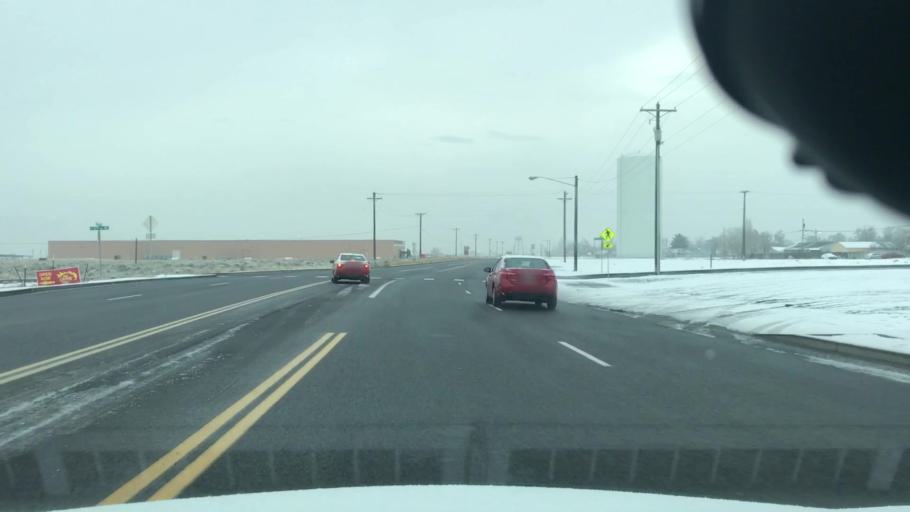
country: US
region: Washington
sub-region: Grant County
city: Moses Lake North
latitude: 47.1746
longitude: -119.3195
